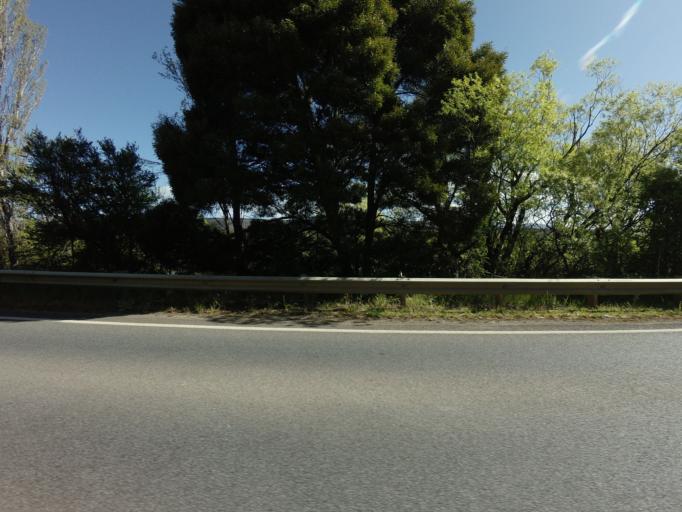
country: AU
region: Tasmania
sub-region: Derwent Valley
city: New Norfolk
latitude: -42.7388
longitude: 146.9797
